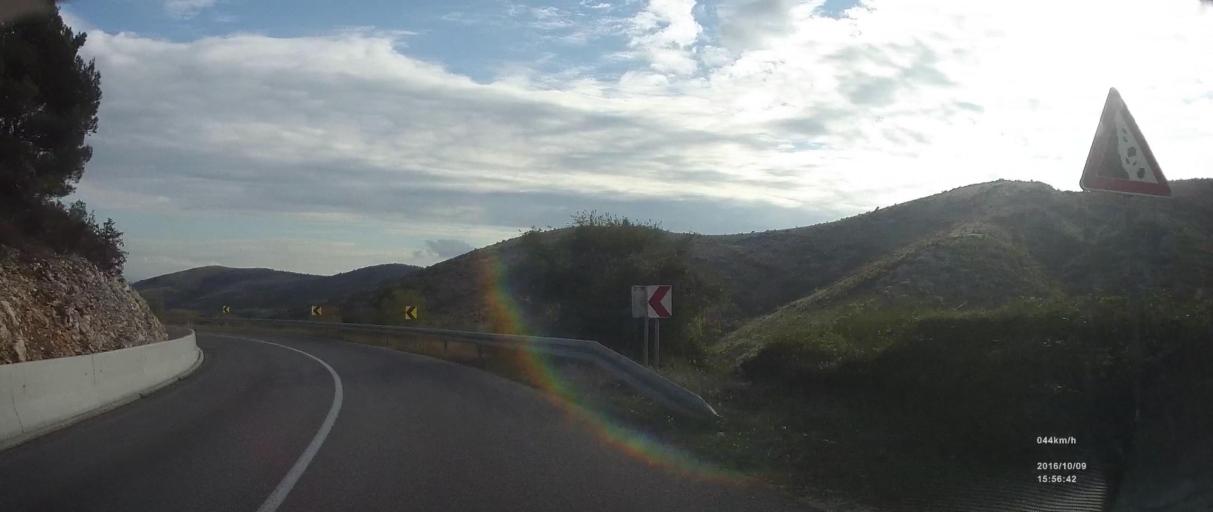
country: HR
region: Splitsko-Dalmatinska
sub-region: Grad Trogir
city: Trogir
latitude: 43.5766
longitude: 16.2325
